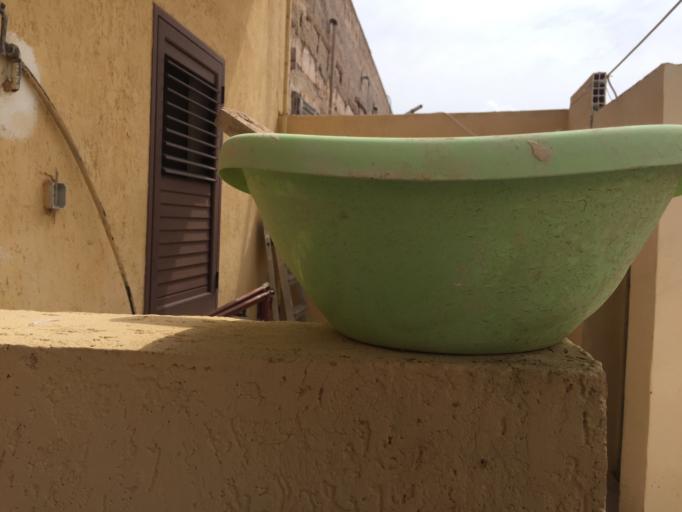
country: IT
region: Sicily
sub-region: Agrigento
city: Lampedusa
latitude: 35.5013
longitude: 12.6122
